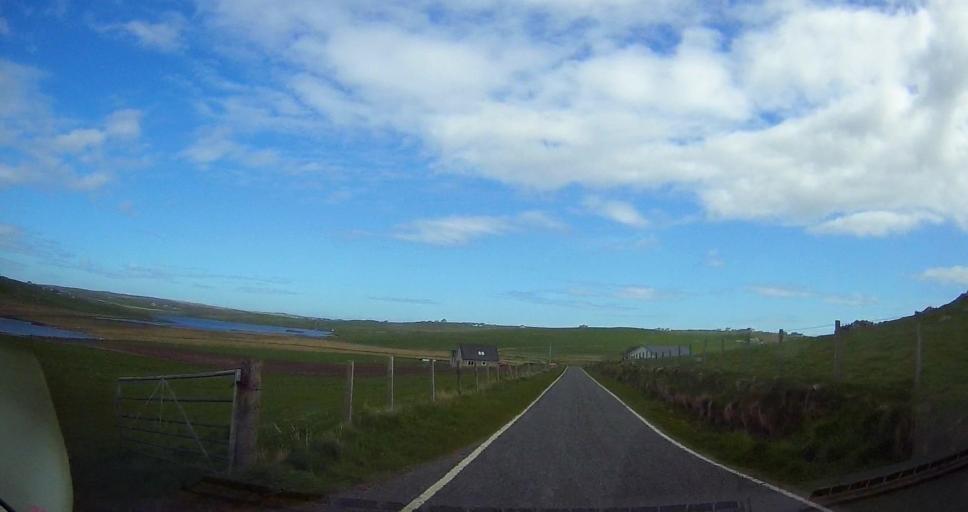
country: GB
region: Scotland
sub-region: Shetland Islands
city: Sandwick
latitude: 59.9240
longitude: -1.3334
